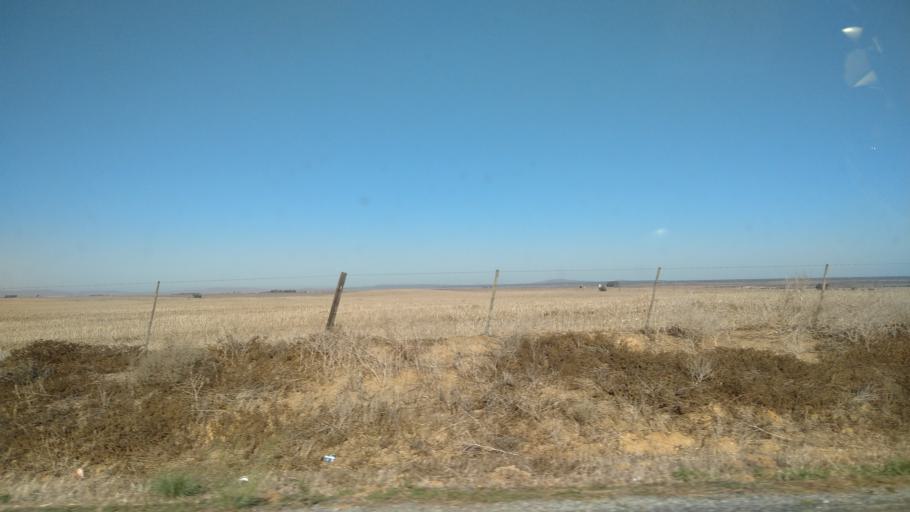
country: ZA
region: Western Cape
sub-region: West Coast District Municipality
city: Moorreesburg
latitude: -33.1605
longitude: 18.4717
